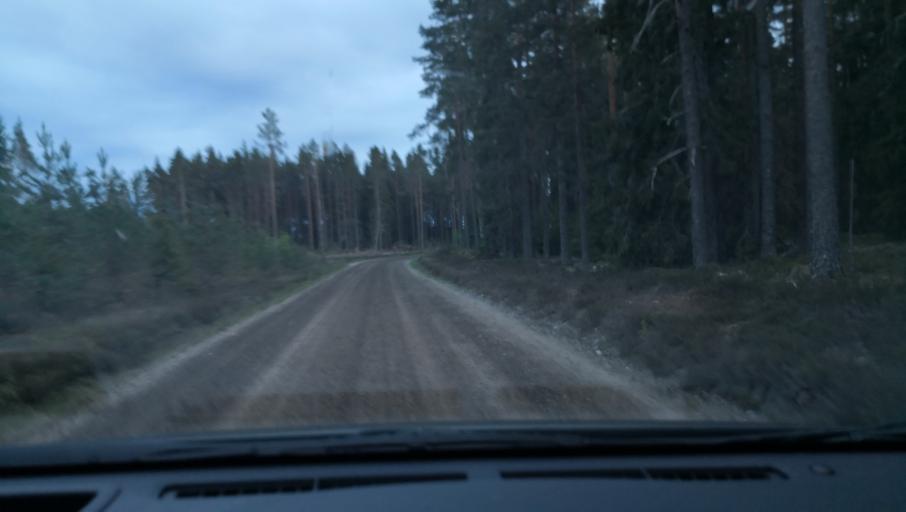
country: SE
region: Vaestmanland
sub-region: Skinnskattebergs Kommun
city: Skinnskatteberg
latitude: 59.7129
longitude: 15.5126
